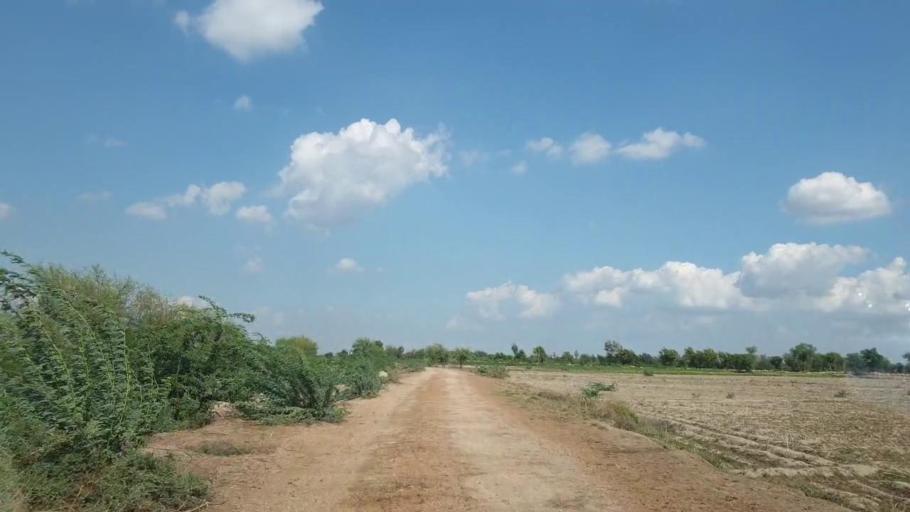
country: PK
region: Sindh
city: Pithoro
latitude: 25.6013
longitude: 69.3878
